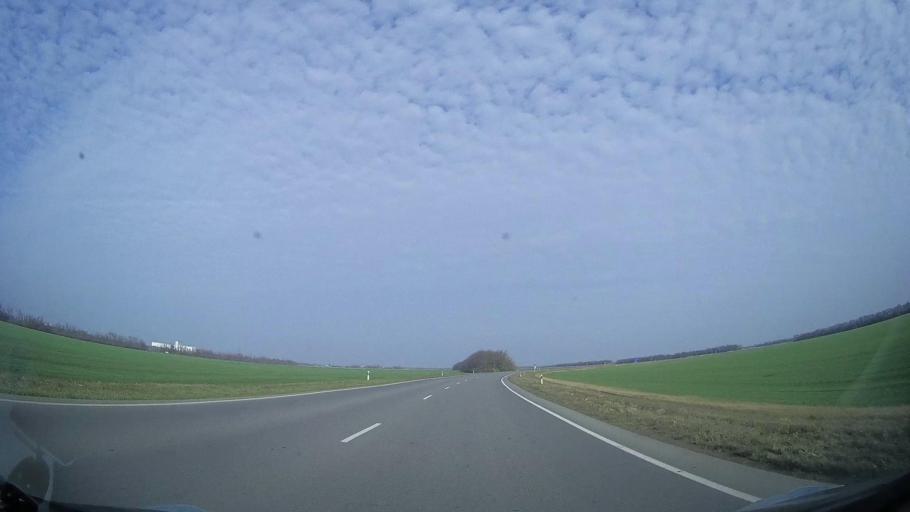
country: RU
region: Rostov
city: Tselina
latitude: 46.5192
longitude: 41.0730
